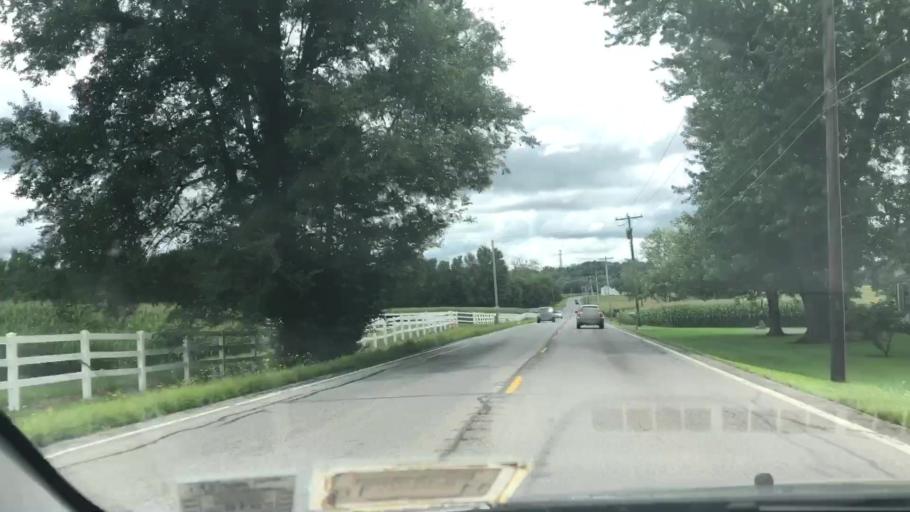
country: US
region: New York
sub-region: Wayne County
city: Macedon
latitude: 43.1039
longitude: -77.2933
